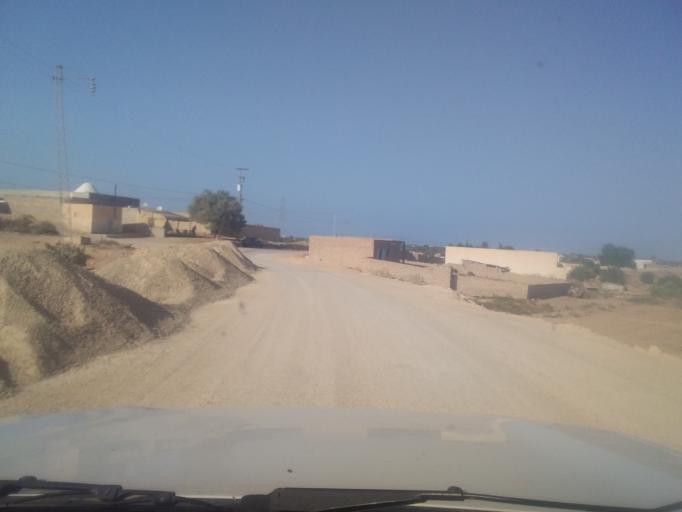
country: TN
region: Qabis
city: Matmata
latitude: 33.5832
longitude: 10.2655
